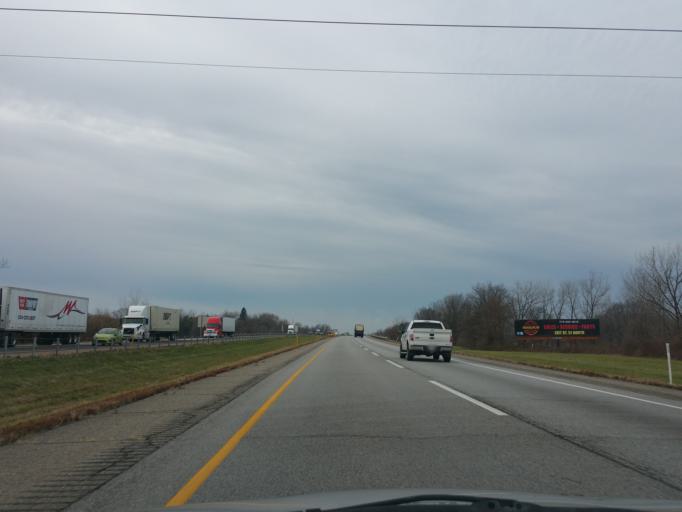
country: US
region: Indiana
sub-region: Porter County
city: Porter
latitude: 41.5791
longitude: -87.0985
